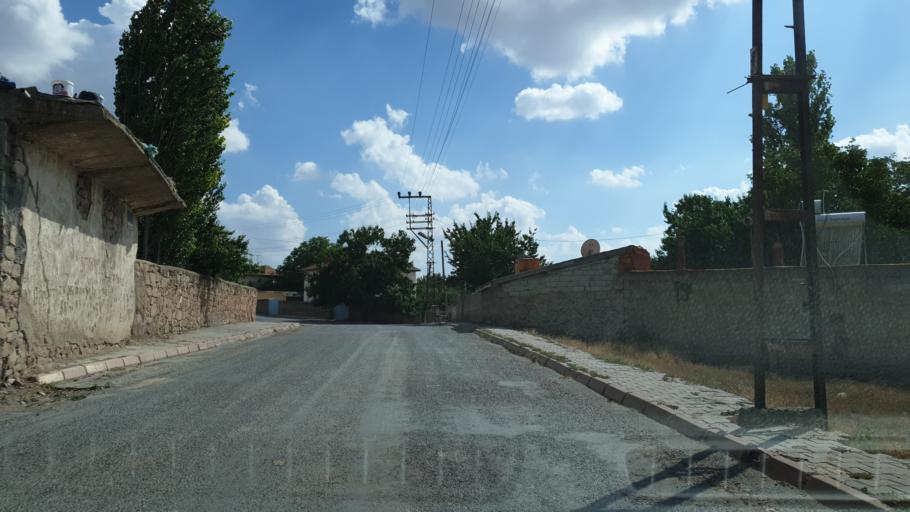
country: TR
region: Kayseri
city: Felahiye
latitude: 39.0906
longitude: 35.5630
